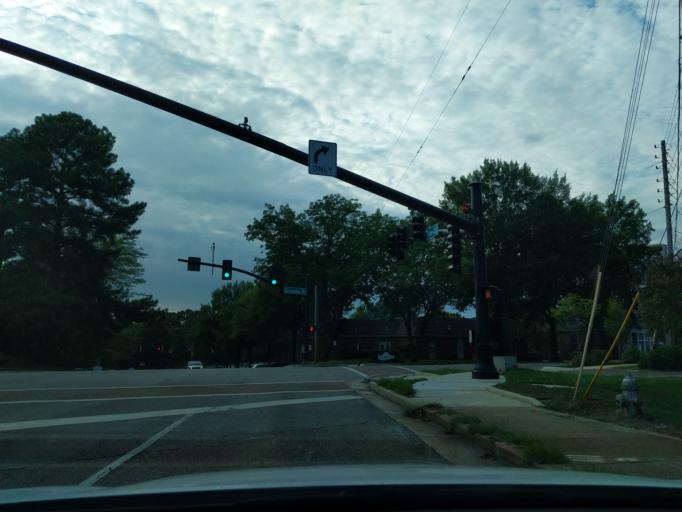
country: US
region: Tennessee
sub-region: Shelby County
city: Germantown
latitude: 35.0845
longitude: -89.8099
